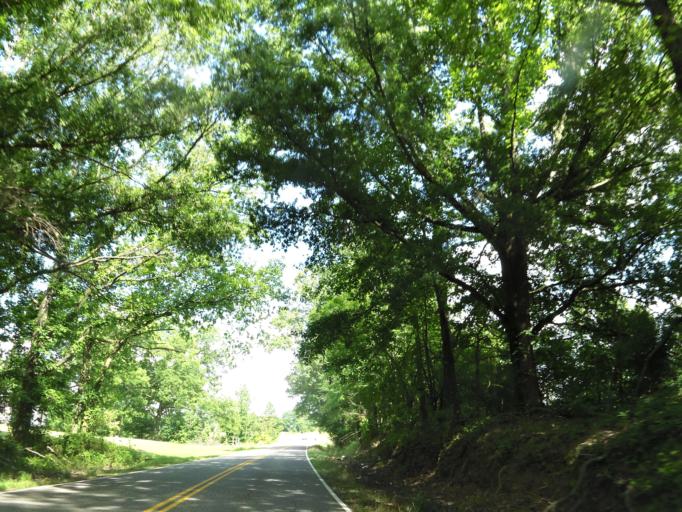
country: US
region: Tennessee
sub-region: Gibson County
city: Milan
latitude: 35.9786
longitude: -88.7592
